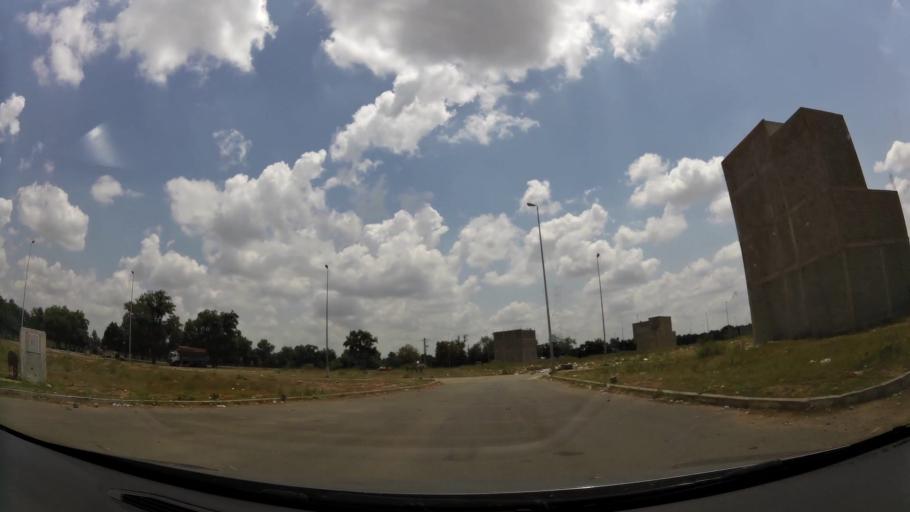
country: MA
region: Rabat-Sale-Zemmour-Zaer
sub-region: Khemisset
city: Tiflet
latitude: 33.9985
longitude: -6.5206
